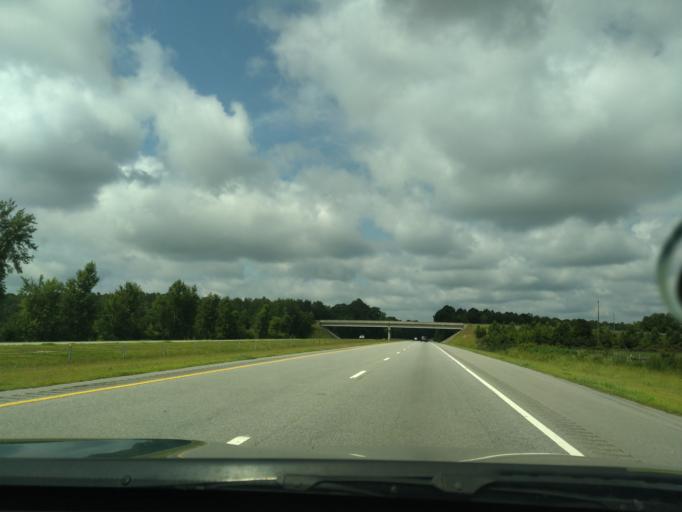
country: US
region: North Carolina
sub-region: Martin County
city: Robersonville
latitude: 35.8264
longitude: -77.1517
